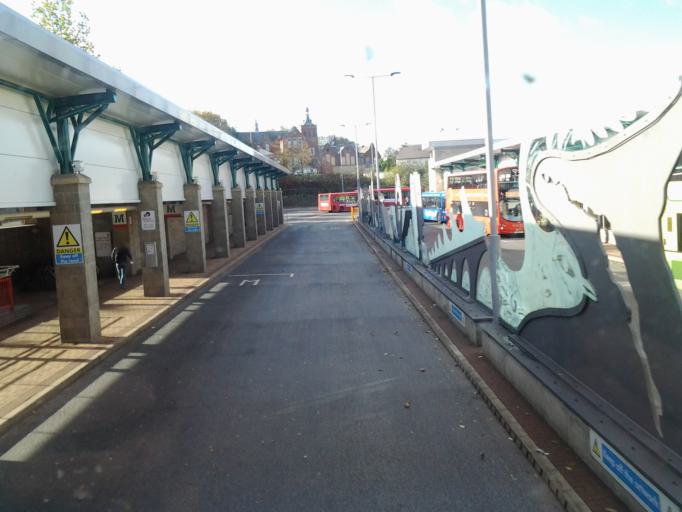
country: GB
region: England
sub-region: Gateshead
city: Gateshead
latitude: 54.9614
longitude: -1.6039
